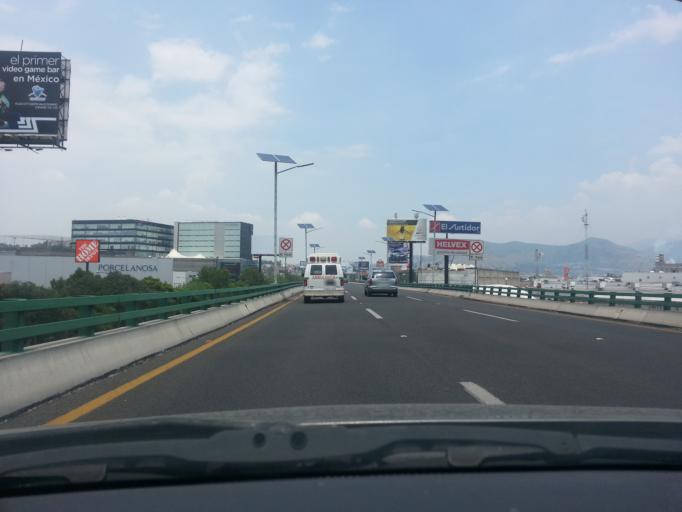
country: MX
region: Mexico
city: Tlalnepantla
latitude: 19.5444
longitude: -99.2117
